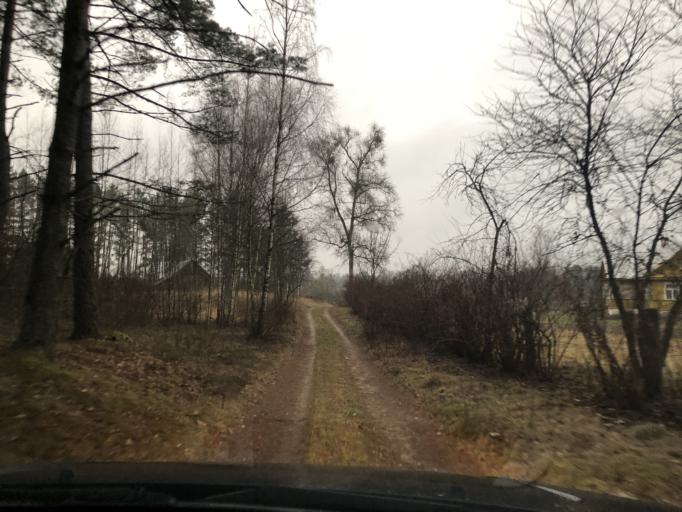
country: LT
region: Alytaus apskritis
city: Druskininkai
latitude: 53.9059
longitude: 24.1785
